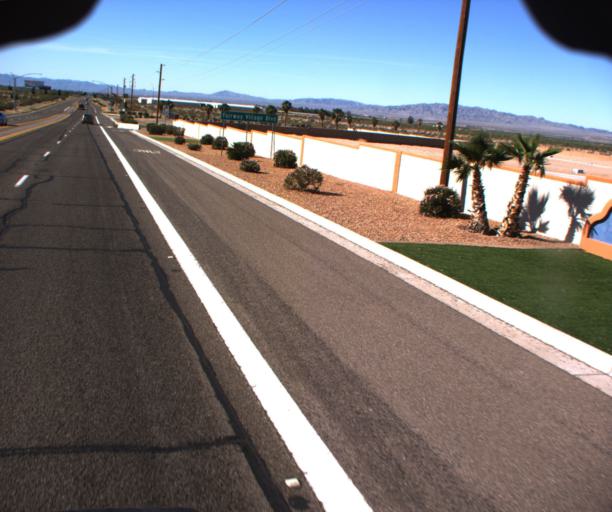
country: US
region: Arizona
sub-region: Mohave County
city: Mohave Valley
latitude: 34.9807
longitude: -114.5981
